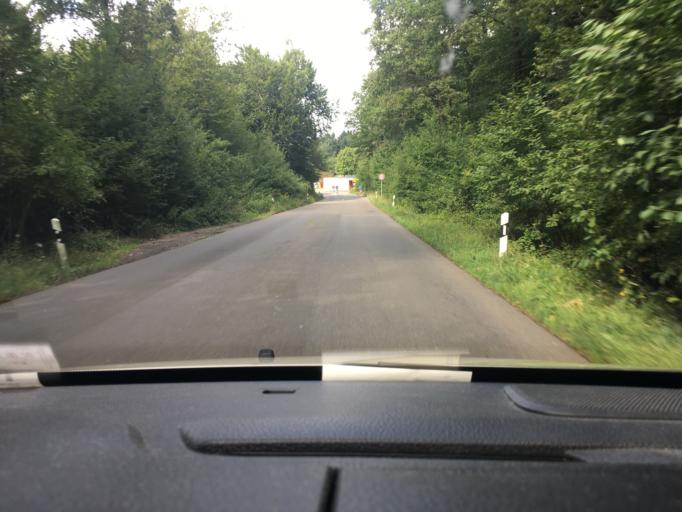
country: DE
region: Saarland
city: Sulzbach
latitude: 49.2799
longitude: 7.0740
